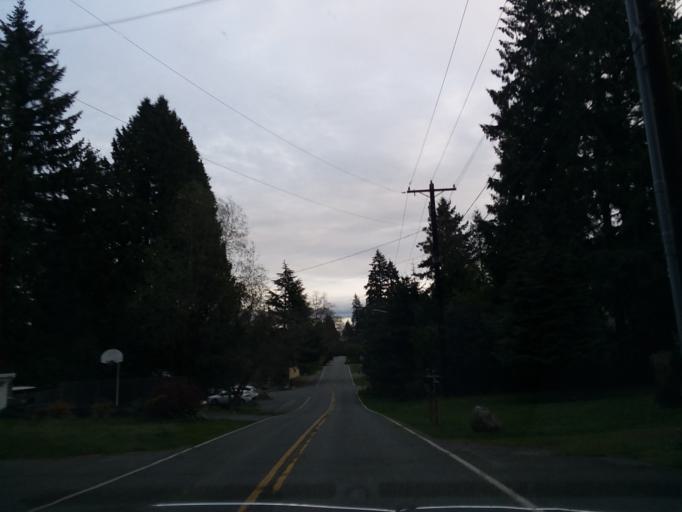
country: US
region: Washington
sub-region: Snohomish County
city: Esperance
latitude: 47.7796
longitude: -122.3542
